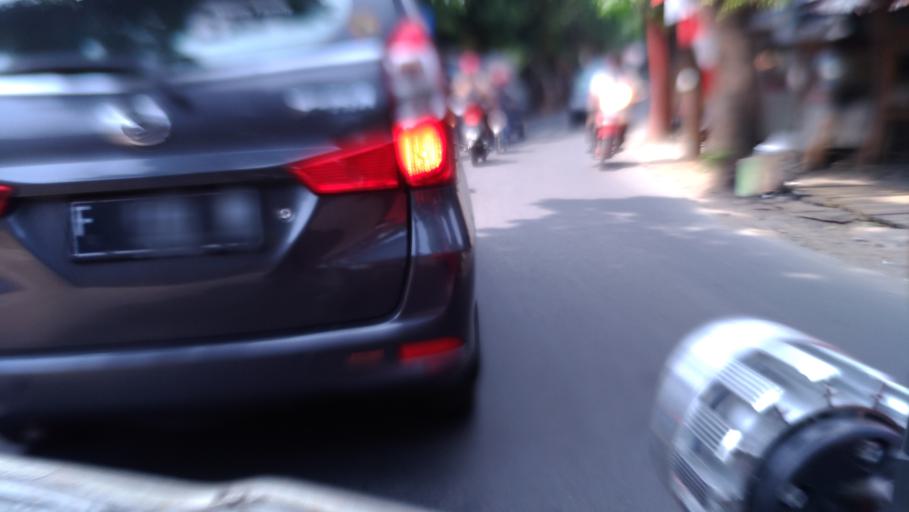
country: ID
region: West Java
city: Cileungsir
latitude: -6.3494
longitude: 106.8937
